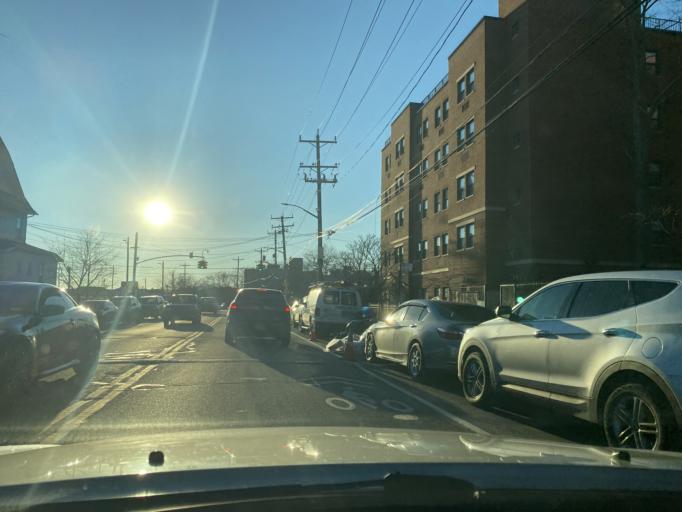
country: US
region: New York
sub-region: Nassau County
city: Inwood
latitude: 40.5990
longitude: -73.7654
